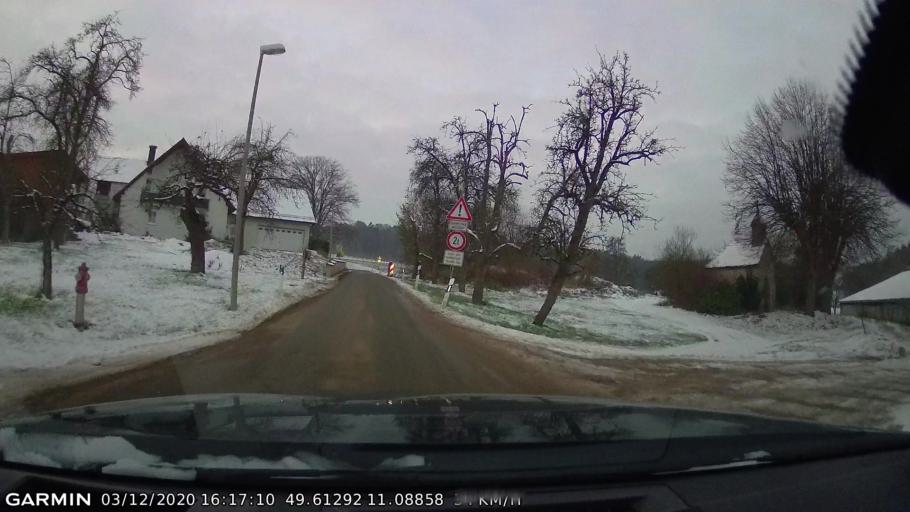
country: DE
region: Bavaria
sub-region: Regierungsbezirk Mittelfranken
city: Uttenreuth
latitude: 49.6130
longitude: 11.0886
